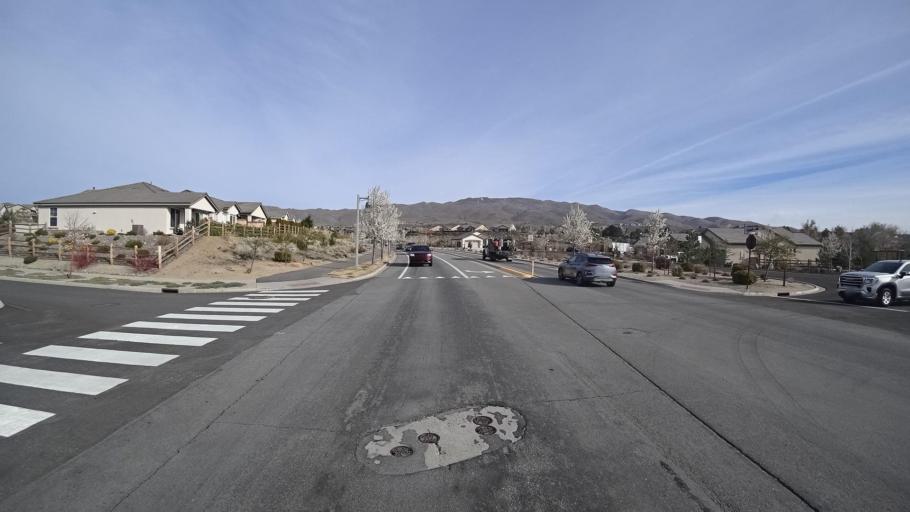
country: US
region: Nevada
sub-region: Washoe County
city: Mogul
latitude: 39.5138
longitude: -119.9416
